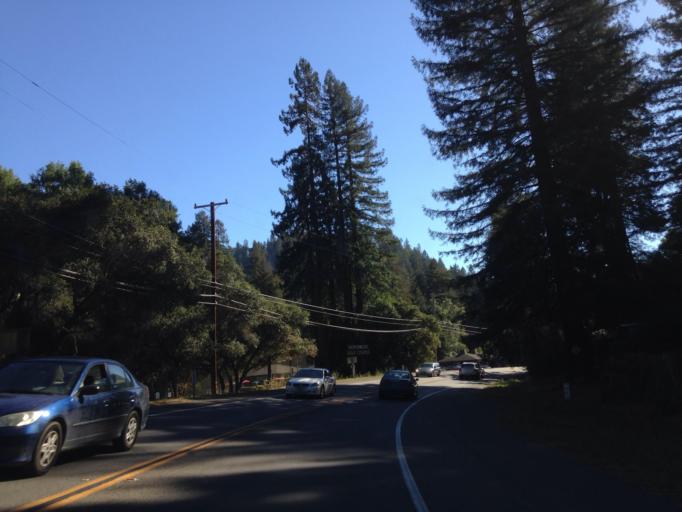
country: US
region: California
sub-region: Sonoma County
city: Monte Rio
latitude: 38.4793
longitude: -122.9968
